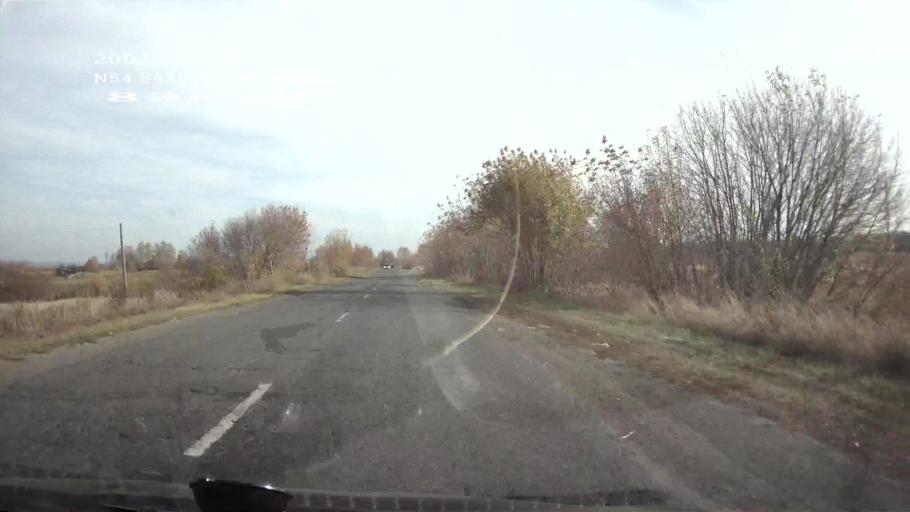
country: RU
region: Chuvashia
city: Alatyr'
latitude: 54.8441
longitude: 46.4684
